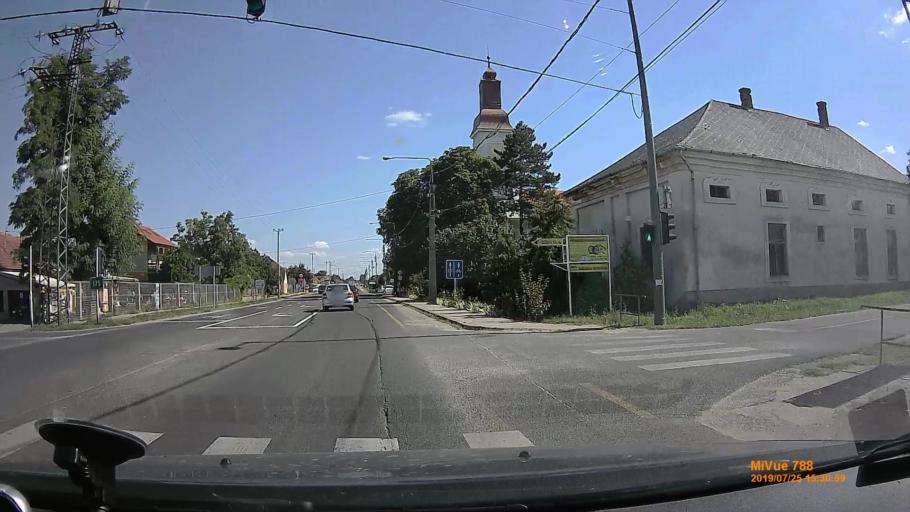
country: HU
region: Borsod-Abauj-Zemplen
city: Malyi
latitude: 48.0163
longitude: 20.8224
